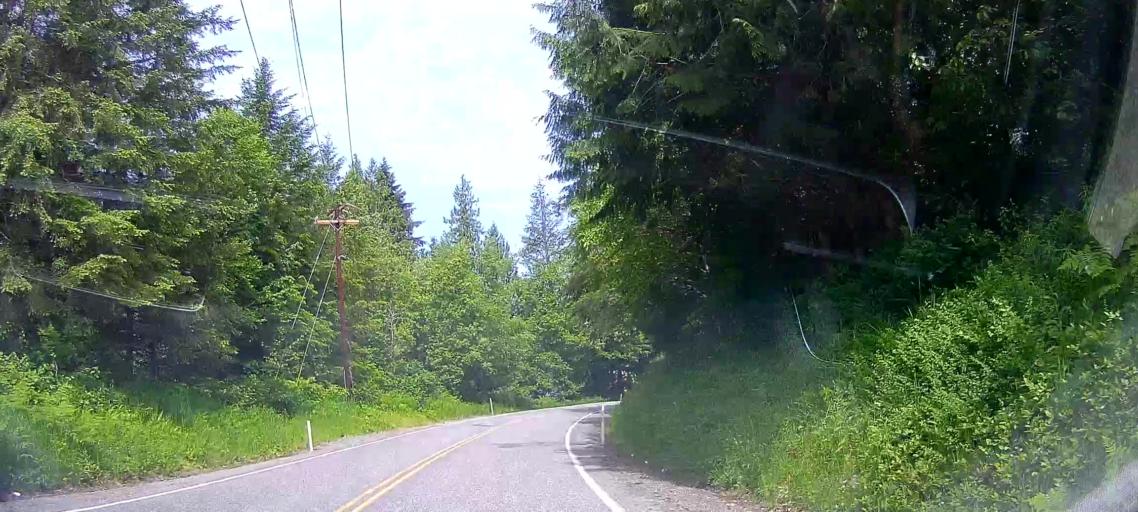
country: US
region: Washington
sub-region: Snohomish County
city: Bryant
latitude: 48.3309
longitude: -122.1661
